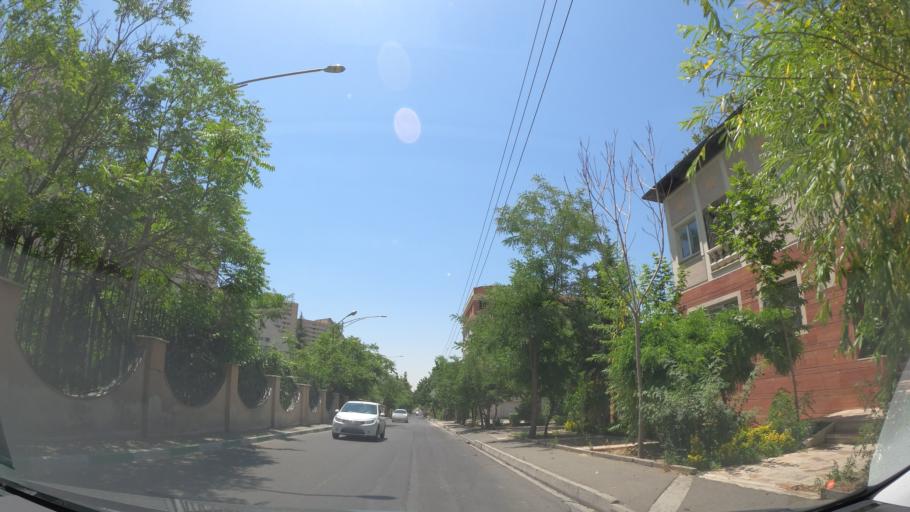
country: IR
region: Tehran
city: Tajrish
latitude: 35.7864
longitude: 51.3884
